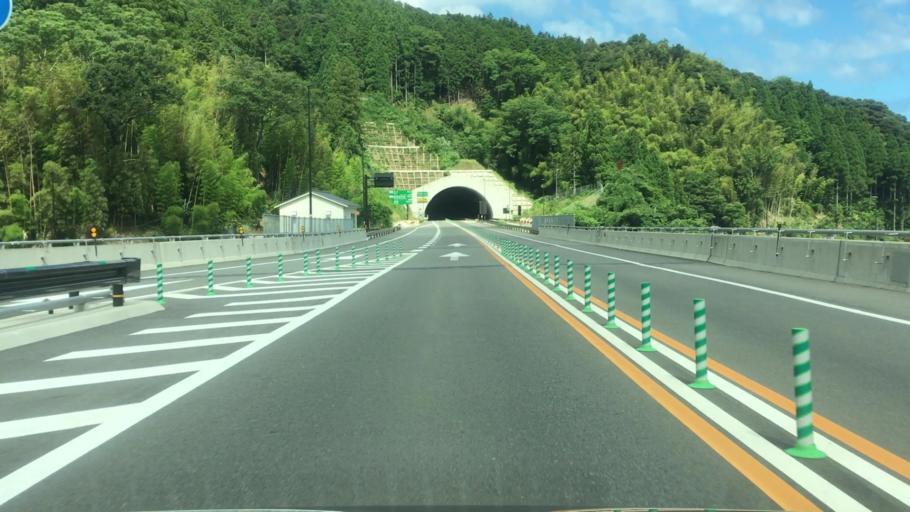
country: JP
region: Hyogo
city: Toyooka
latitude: 35.6386
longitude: 134.5650
